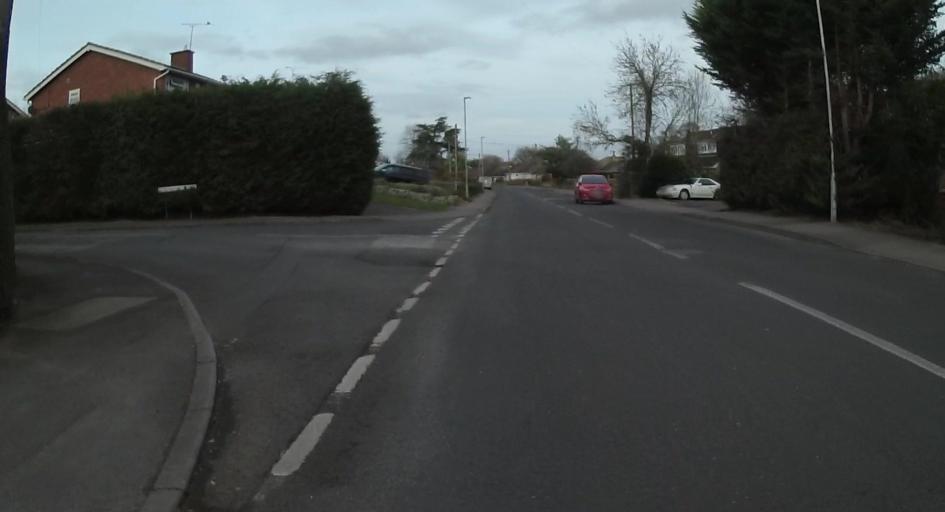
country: GB
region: England
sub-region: Wokingham
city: Woodley
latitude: 51.4414
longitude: -0.8964
